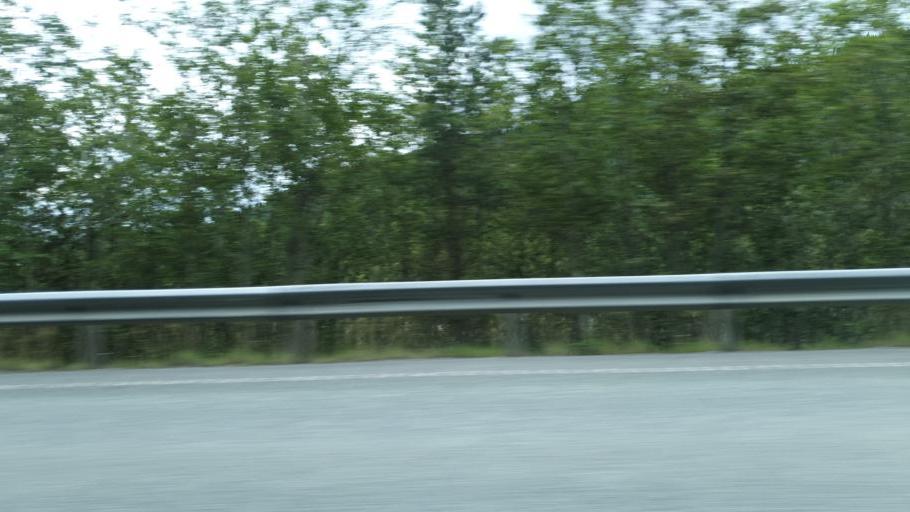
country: NO
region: Sor-Trondelag
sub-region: Midtre Gauldal
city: Storen
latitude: 63.0558
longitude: 10.2941
